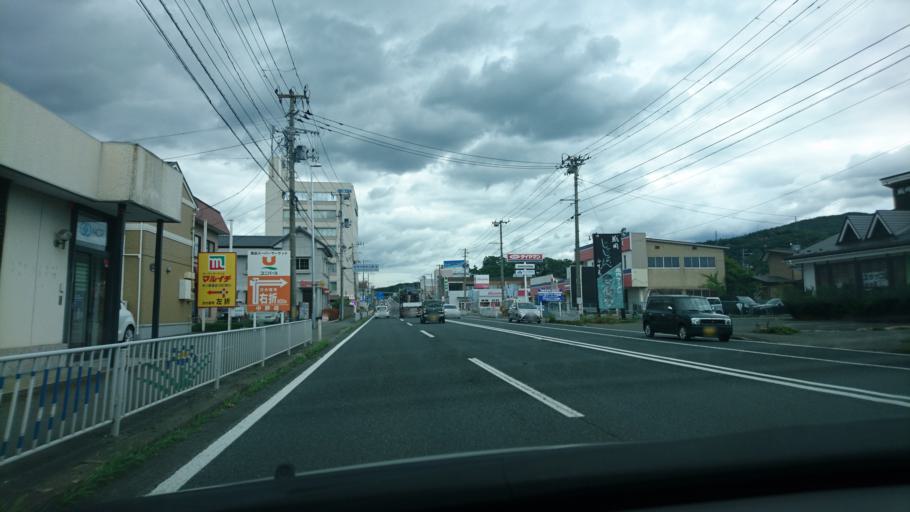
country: JP
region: Iwate
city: Morioka-shi
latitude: 39.6928
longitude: 141.1664
